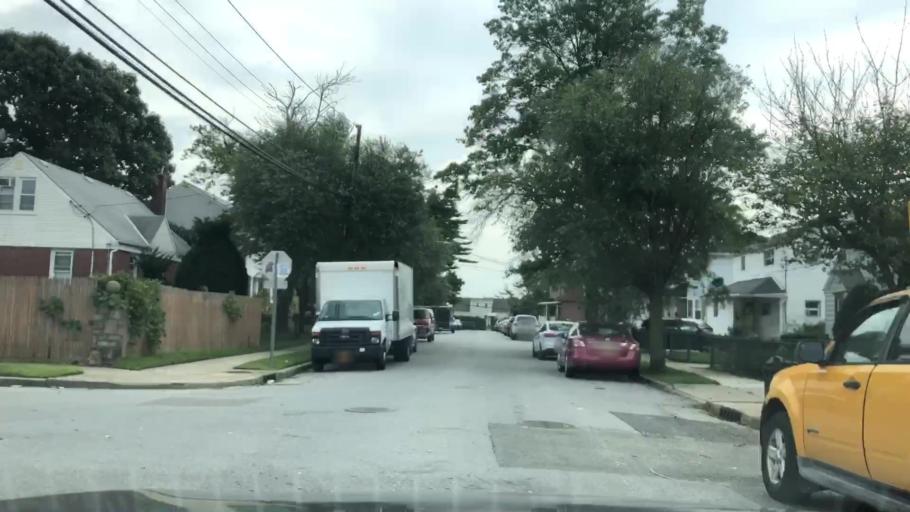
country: US
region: New York
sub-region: Nassau County
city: South Floral Park
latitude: 40.7025
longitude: -73.6914
